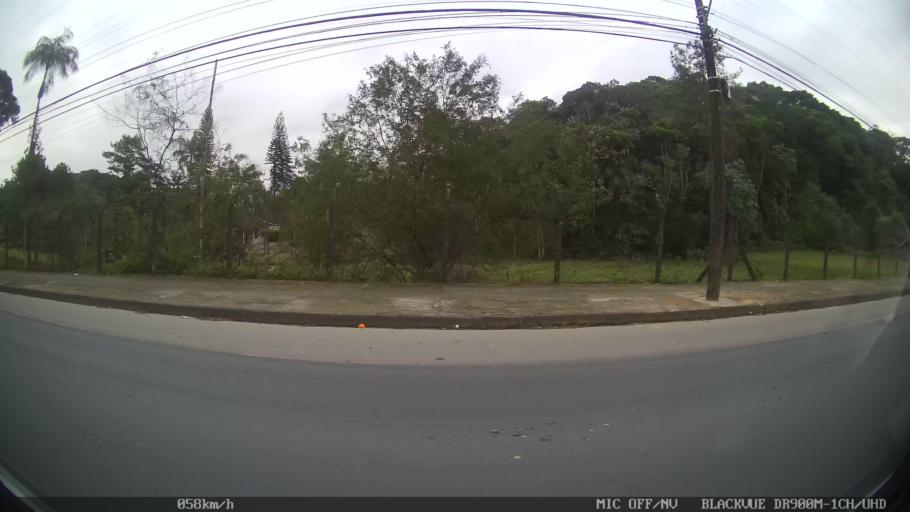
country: BR
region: Santa Catarina
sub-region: Joinville
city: Joinville
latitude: -26.2835
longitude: -48.8862
